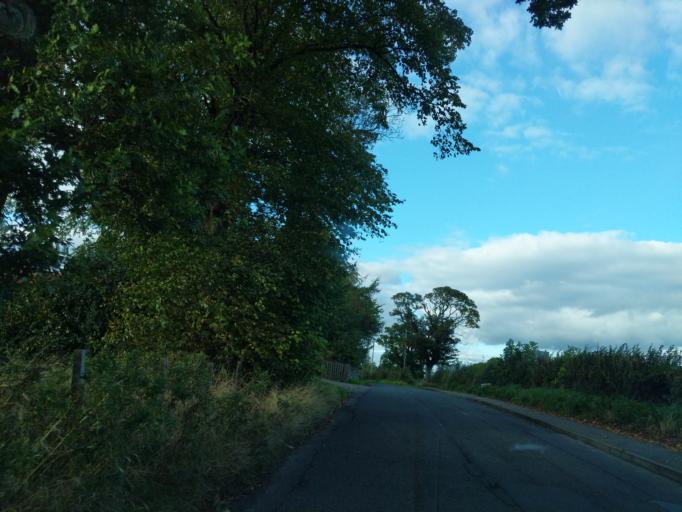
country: GB
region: Scotland
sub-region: Edinburgh
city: Queensferry
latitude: 55.9879
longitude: -3.3770
